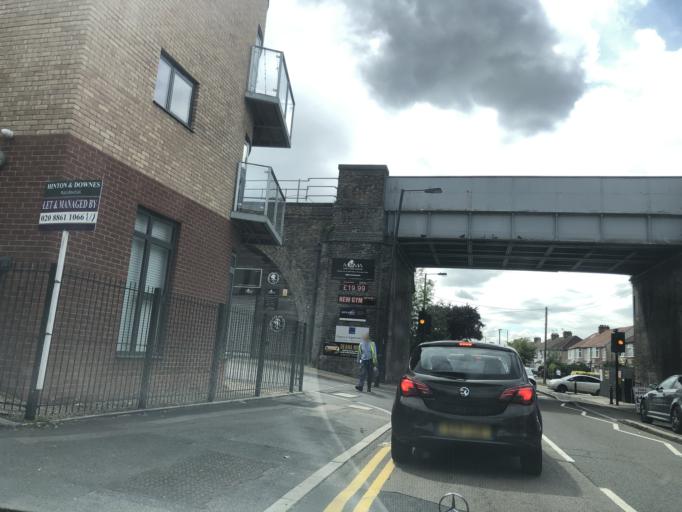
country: GB
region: England
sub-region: Greater London
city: Northolt
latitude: 51.5683
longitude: -0.3563
